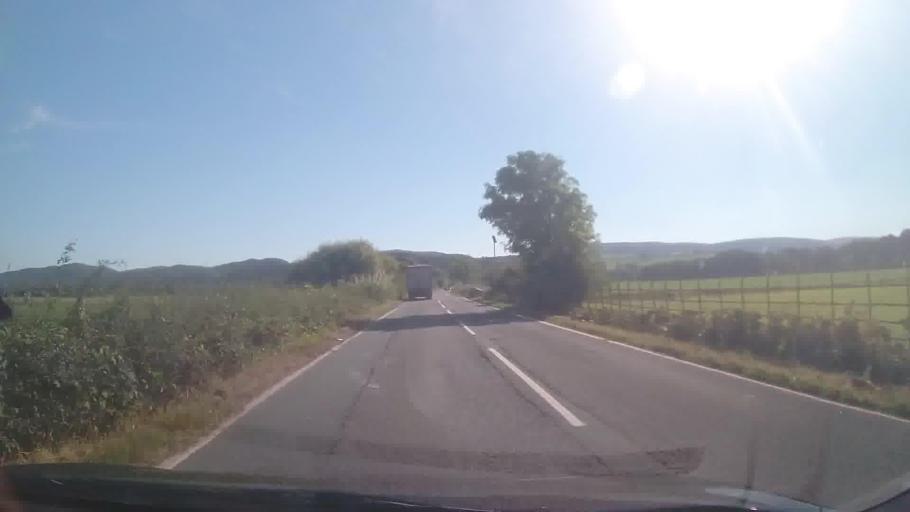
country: GB
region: England
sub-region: Cumbria
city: Askam in Furness
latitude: 54.2692
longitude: -3.1942
